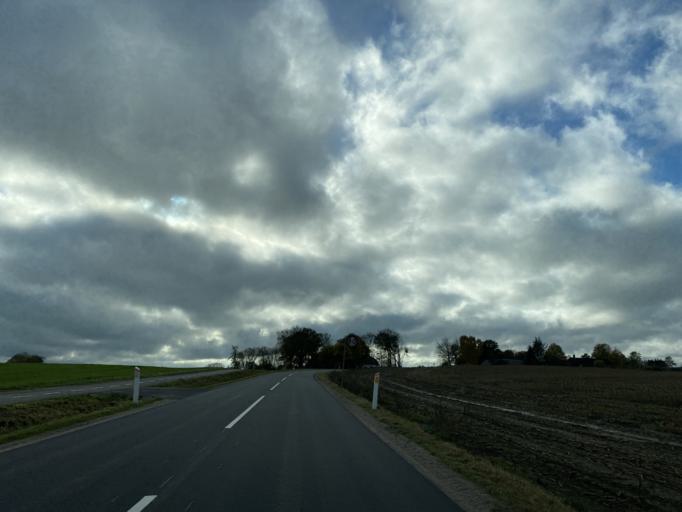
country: DK
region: Central Jutland
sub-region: Favrskov Kommune
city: Hammel
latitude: 56.2483
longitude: 9.8254
